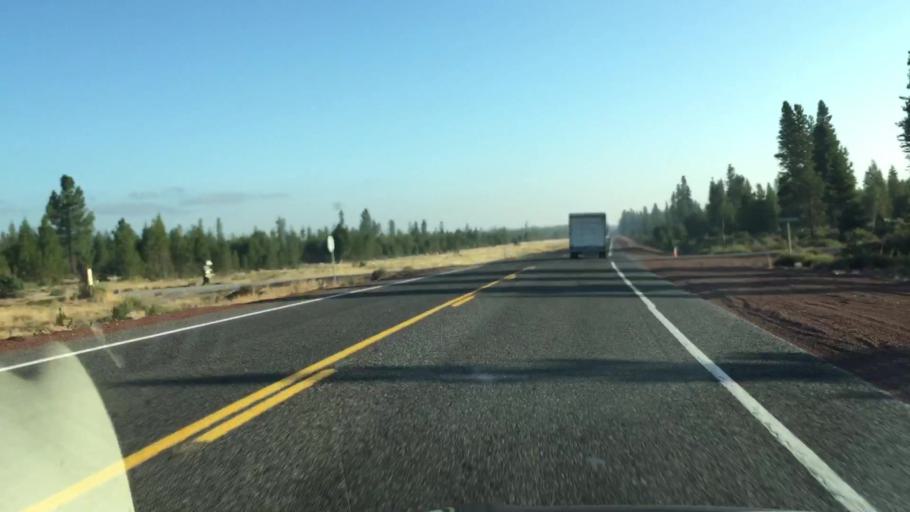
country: US
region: Oregon
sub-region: Deschutes County
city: La Pine
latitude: 43.4296
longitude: -121.7152
